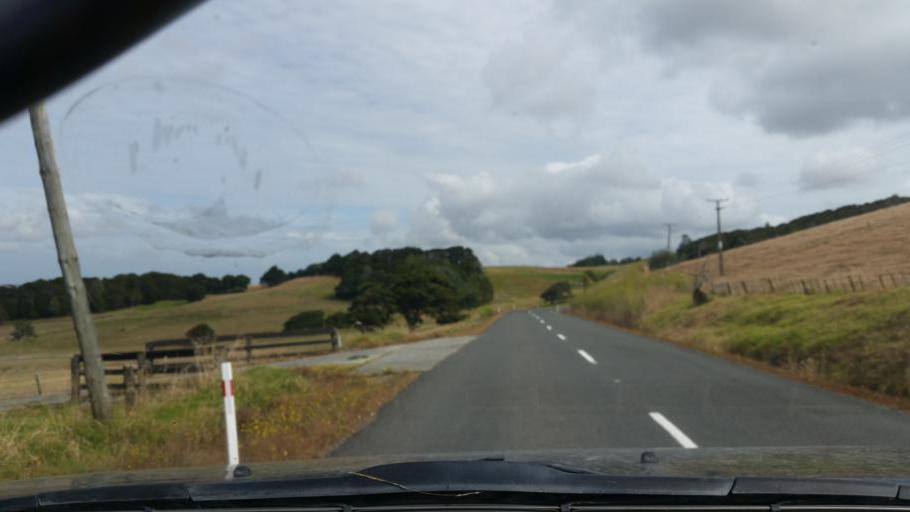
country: NZ
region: Northland
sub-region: Kaipara District
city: Dargaville
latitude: -35.9623
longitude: 173.9274
